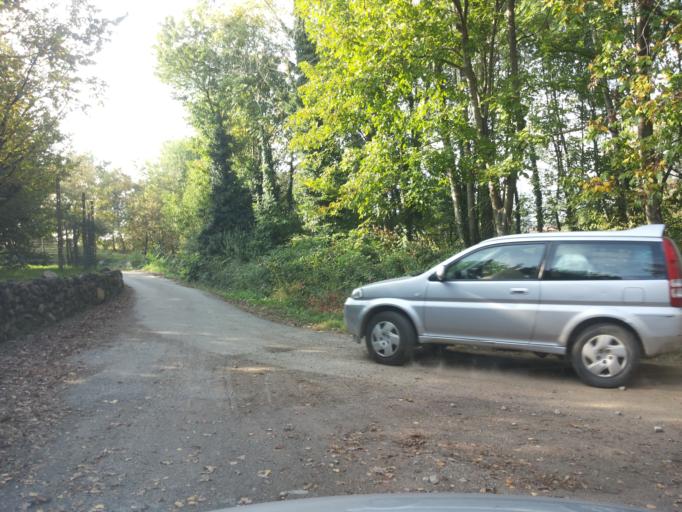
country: IT
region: Piedmont
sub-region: Provincia di Biella
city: Viverone
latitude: 45.4342
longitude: 8.0441
